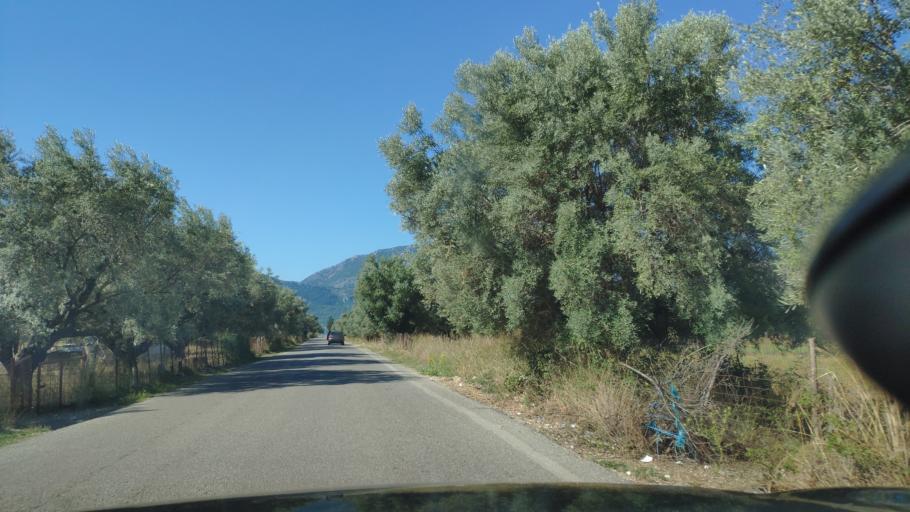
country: GR
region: West Greece
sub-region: Nomos Aitolias kai Akarnanias
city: Kandila
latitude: 38.6892
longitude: 20.9450
